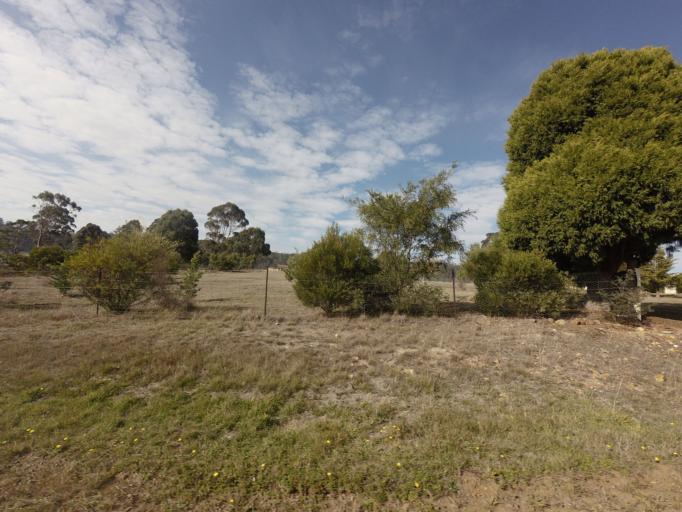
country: AU
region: Tasmania
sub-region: Sorell
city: Sorell
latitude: -42.4830
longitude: 147.4801
